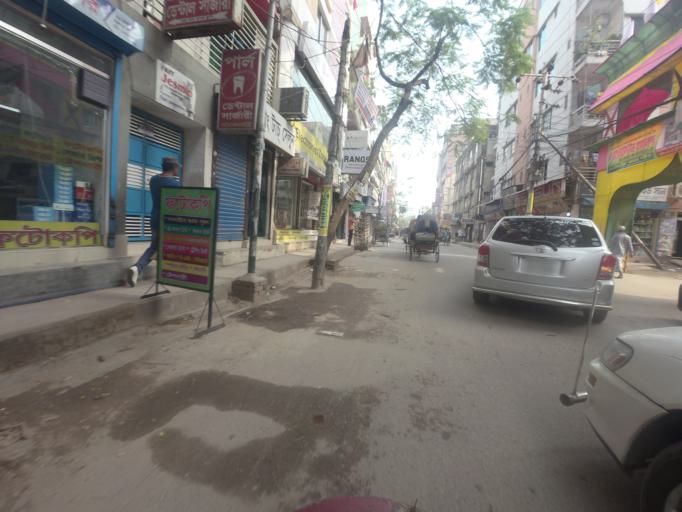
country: BD
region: Dhaka
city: Azimpur
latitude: 23.7607
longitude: 90.3617
